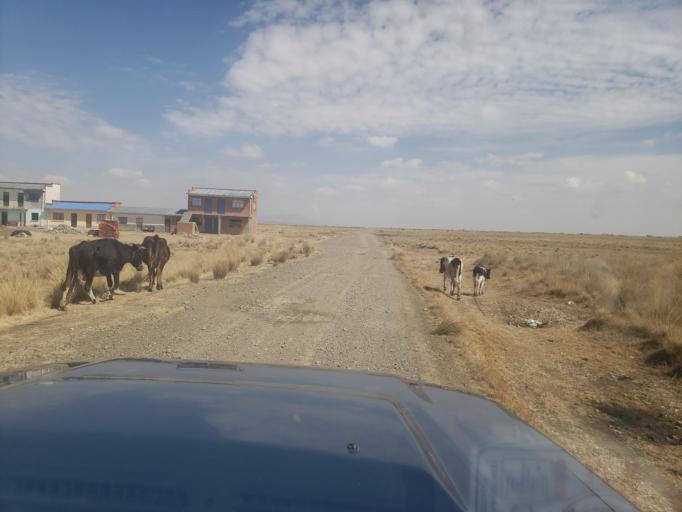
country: BO
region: La Paz
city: Batallas
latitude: -16.4262
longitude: -68.4001
